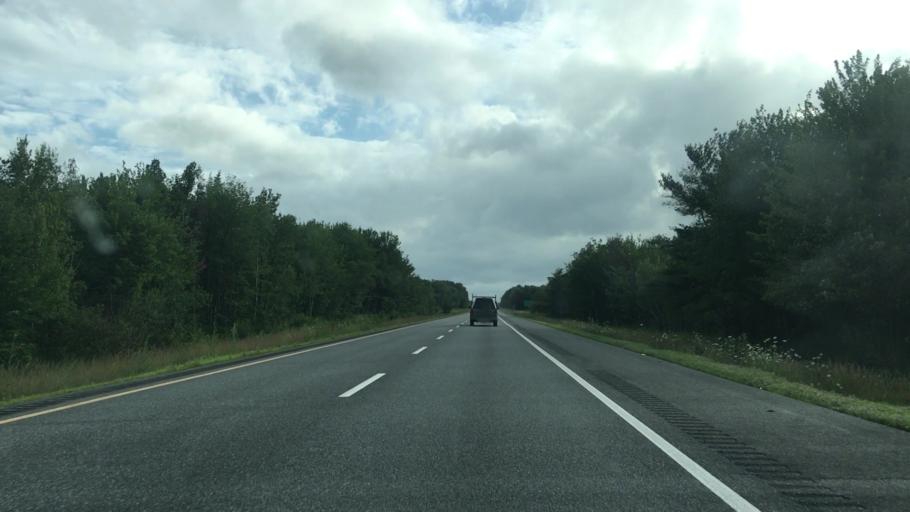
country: US
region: Maine
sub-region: Kennebec County
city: Benton
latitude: 44.6112
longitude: -69.5683
